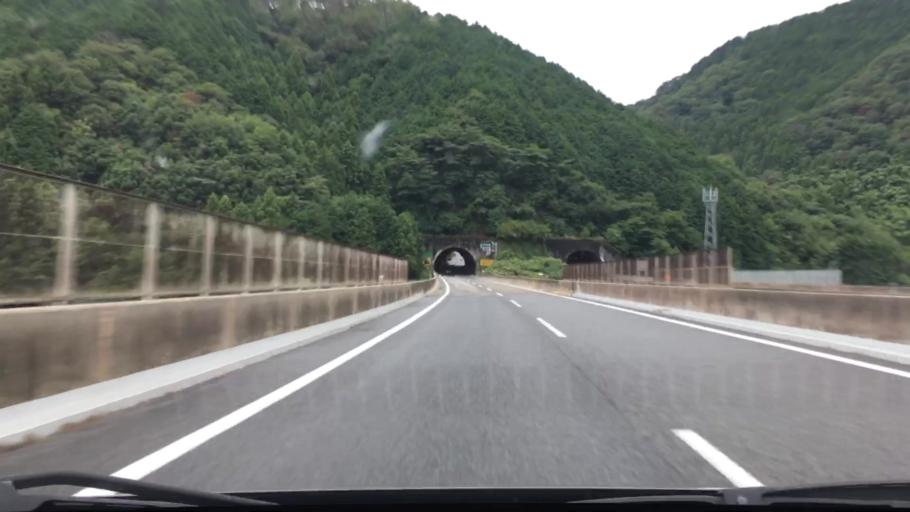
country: JP
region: Hiroshima
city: Hiroshima-shi
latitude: 34.5285
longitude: 132.4335
